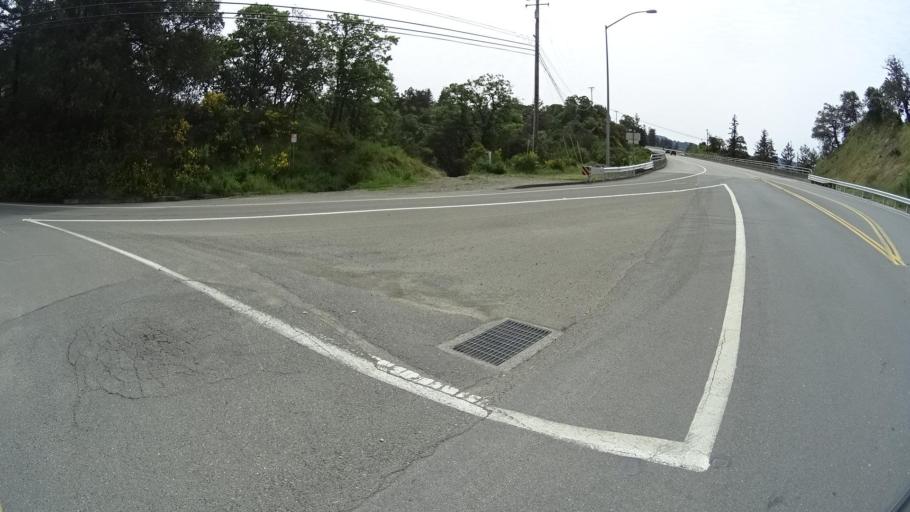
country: US
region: California
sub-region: Humboldt County
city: Redway
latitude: 40.1078
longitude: -123.7959
